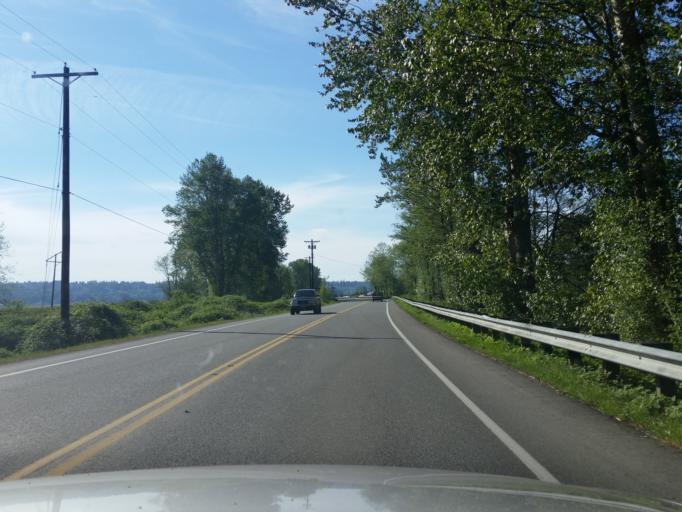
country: US
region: Washington
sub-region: Snohomish County
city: Snohomish
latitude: 47.9122
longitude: -122.1162
